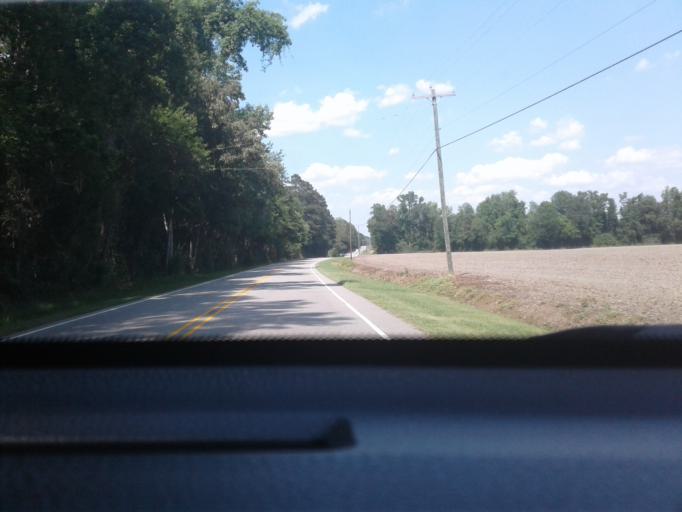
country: US
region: North Carolina
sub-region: Cumberland County
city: Eastover
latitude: 35.1754
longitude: -78.7184
